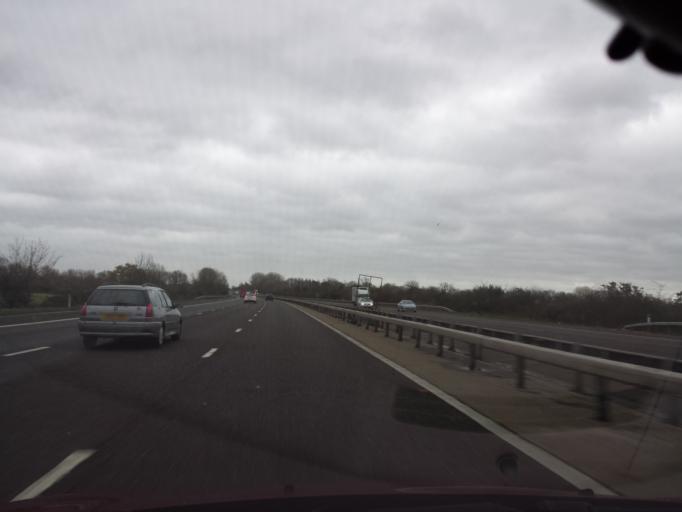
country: GB
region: England
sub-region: Surrey
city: Chertsey
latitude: 51.3961
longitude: -0.4995
